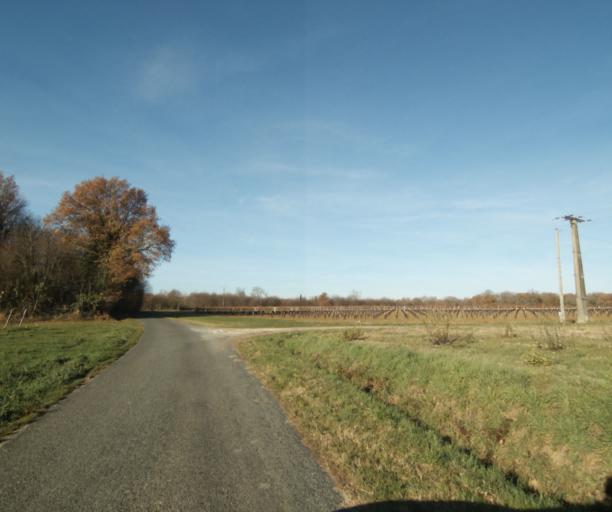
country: FR
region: Poitou-Charentes
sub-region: Departement de la Charente-Maritime
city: Cherac
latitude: 45.7346
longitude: -0.4589
